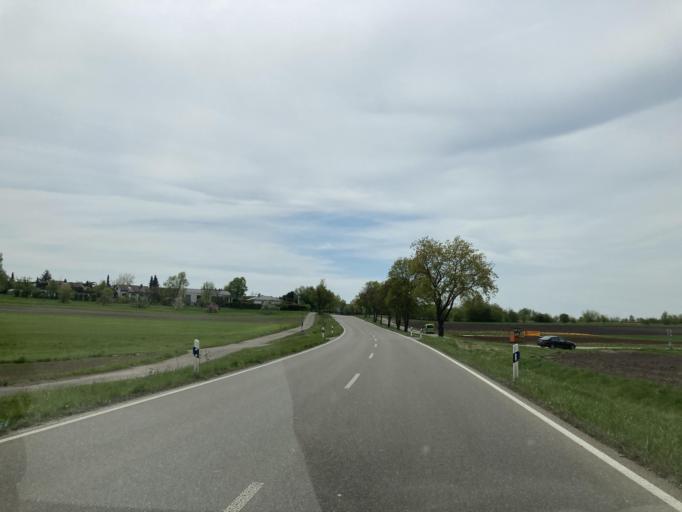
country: DE
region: Baden-Wuerttemberg
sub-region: Tuebingen Region
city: Rottenburg
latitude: 48.5117
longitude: 8.9707
